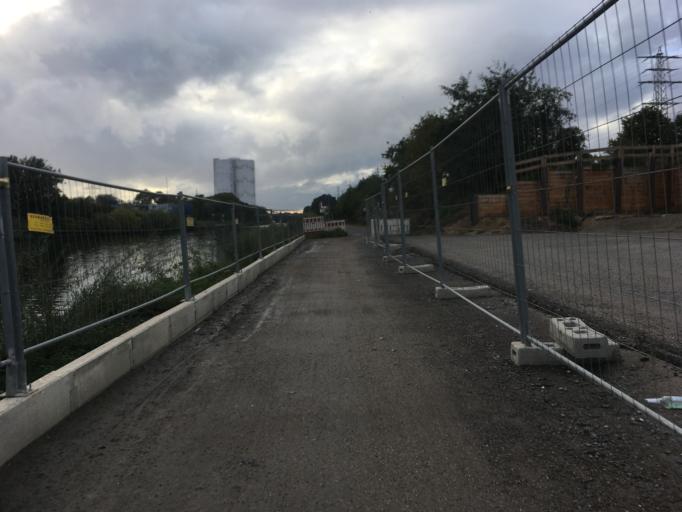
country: DE
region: North Rhine-Westphalia
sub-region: Regierungsbezirk Dusseldorf
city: Oberhausen
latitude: 51.4953
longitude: 6.8864
